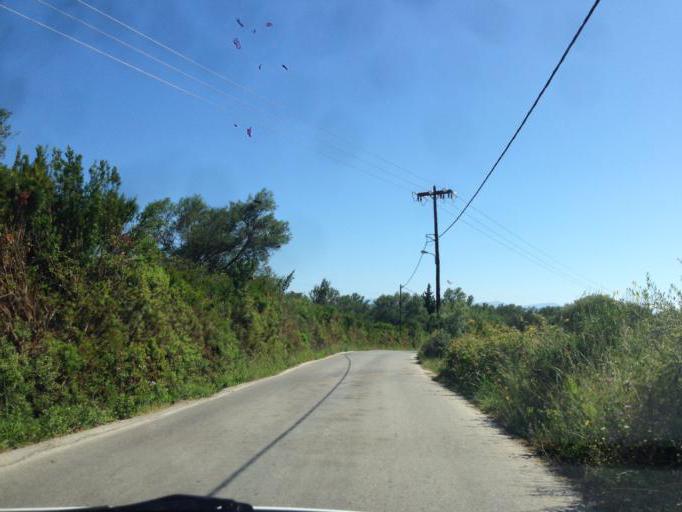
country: GR
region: Ionian Islands
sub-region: Nomos Kerkyras
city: Acharavi
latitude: 39.7914
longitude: 19.7806
